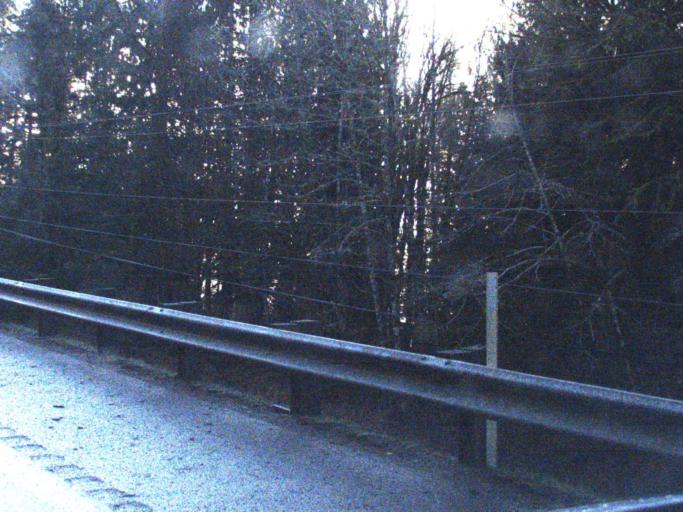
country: US
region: Washington
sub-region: Snohomish County
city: Darrington
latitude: 48.5124
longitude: -121.6678
